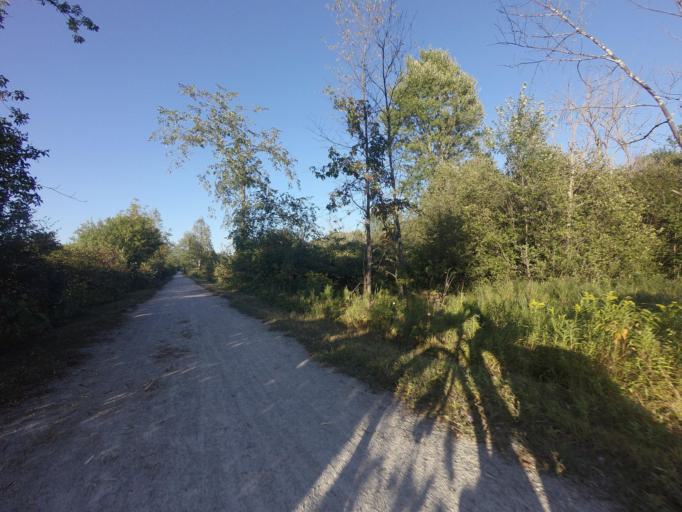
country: CA
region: Ontario
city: Orangeville
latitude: 43.8189
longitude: -79.9240
